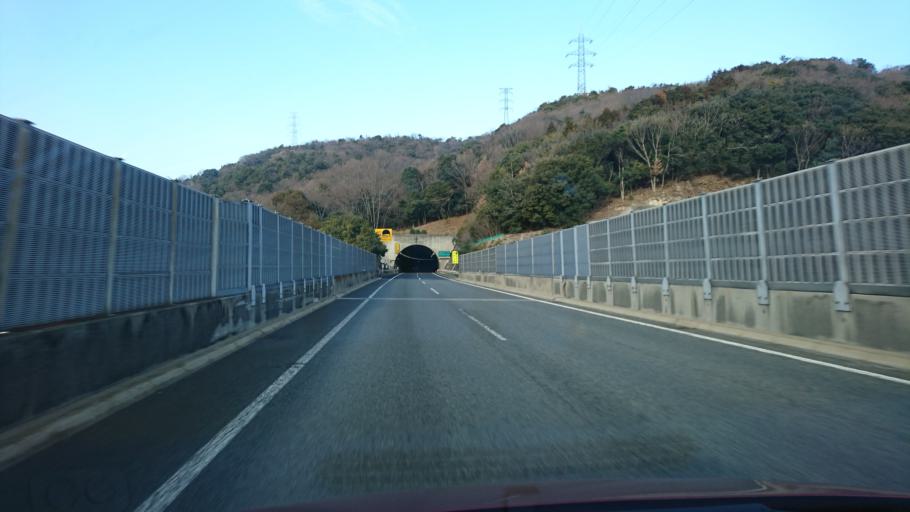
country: JP
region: Hyogo
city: Himeji
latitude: 34.8606
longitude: 134.7199
